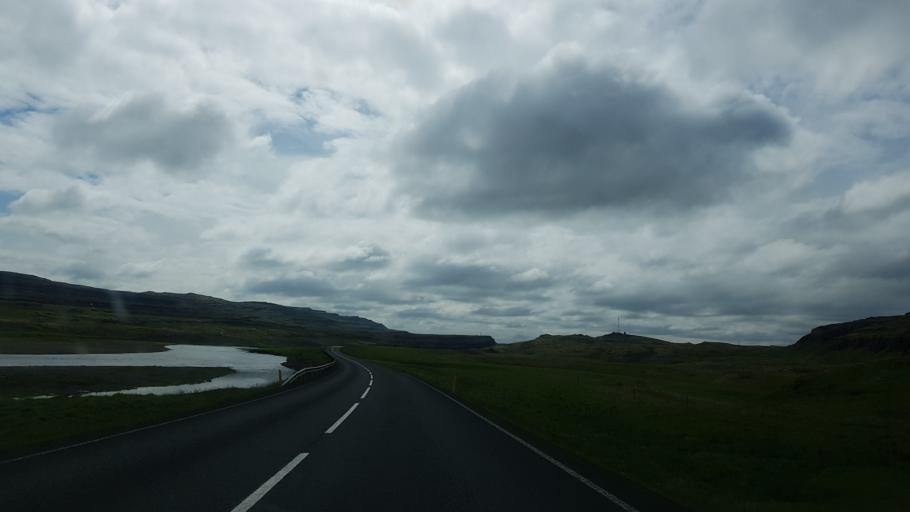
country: IS
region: West
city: Borgarnes
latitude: 64.8142
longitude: -21.4119
